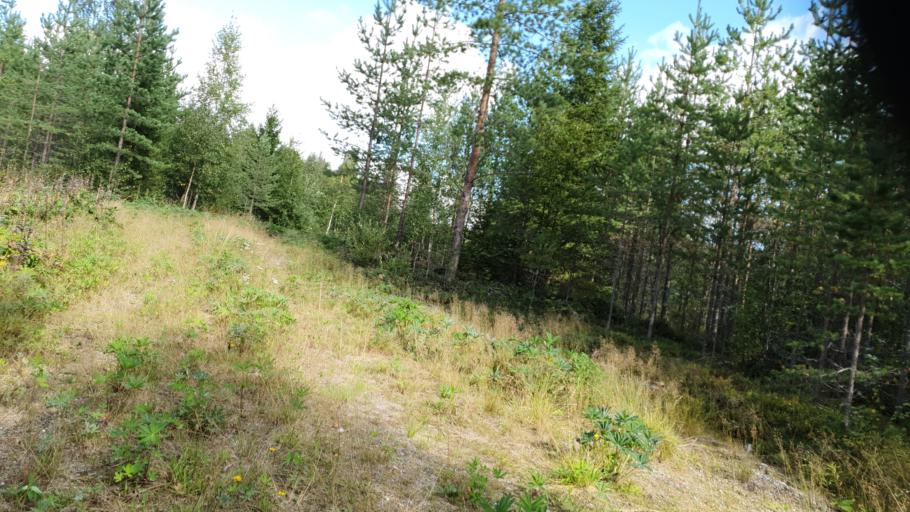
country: FI
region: Kainuu
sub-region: Kehys-Kainuu
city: Kuhmo
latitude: 64.1457
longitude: 29.3540
